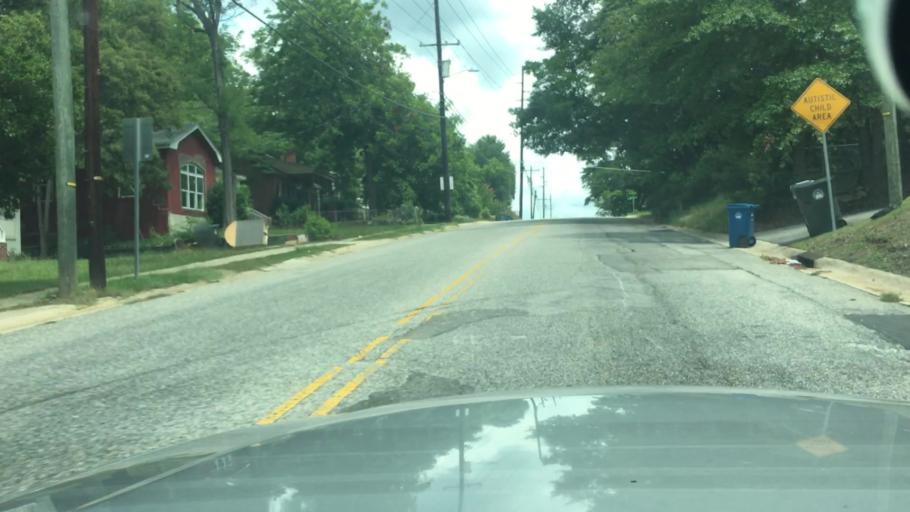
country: US
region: North Carolina
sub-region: Cumberland County
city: Fayetteville
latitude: 35.0801
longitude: -78.8851
